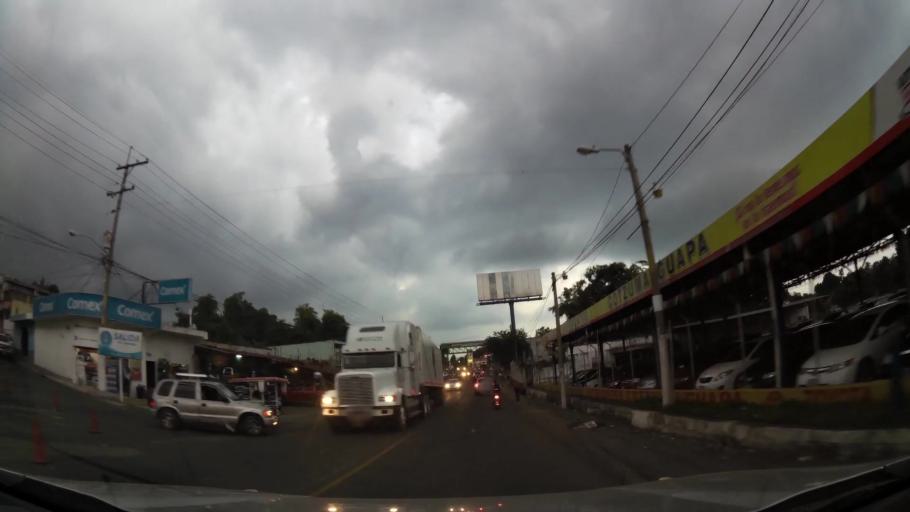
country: GT
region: Escuintla
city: Santa Lucia Cotzumalguapa
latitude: 14.3280
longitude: -91.0252
